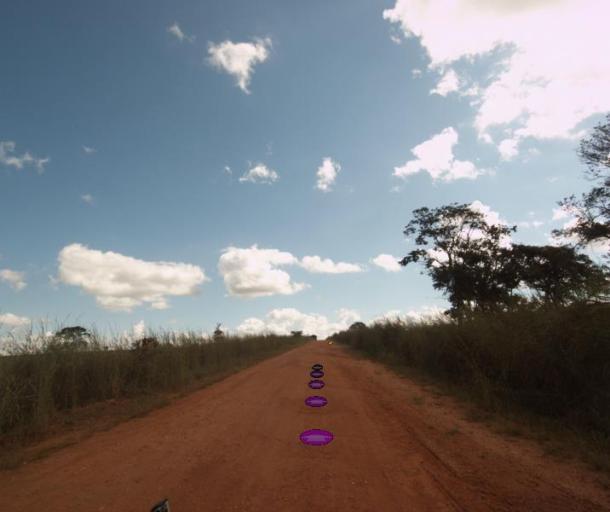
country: BR
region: Goias
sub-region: Jaragua
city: Jaragua
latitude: -15.8300
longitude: -49.2555
